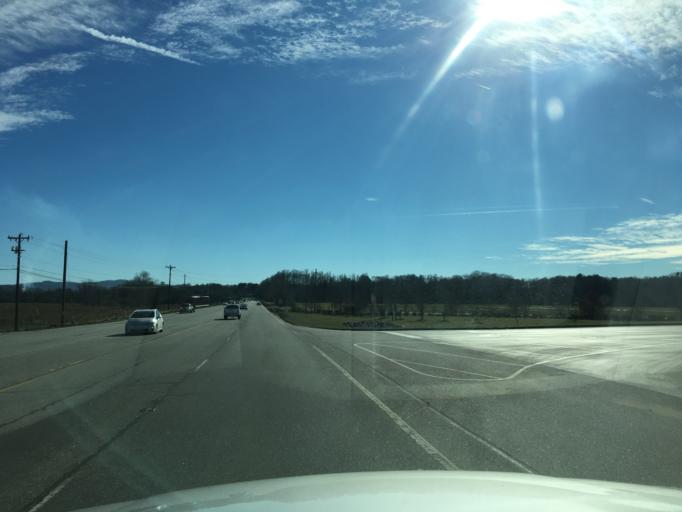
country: US
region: North Carolina
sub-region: Henderson County
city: Mills River
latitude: 35.3990
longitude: -82.5701
